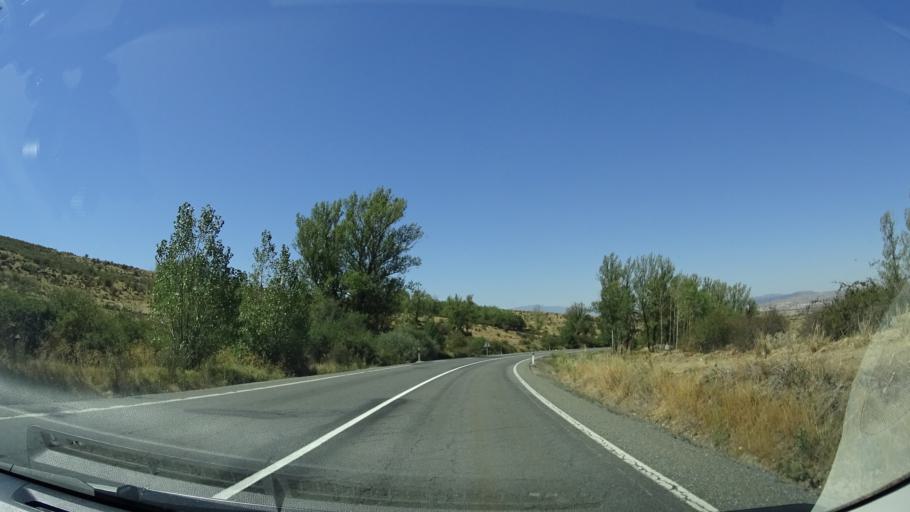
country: ES
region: Castille and Leon
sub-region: Provincia de Avila
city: Tornadizos de Avila
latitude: 40.6187
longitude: -4.5984
